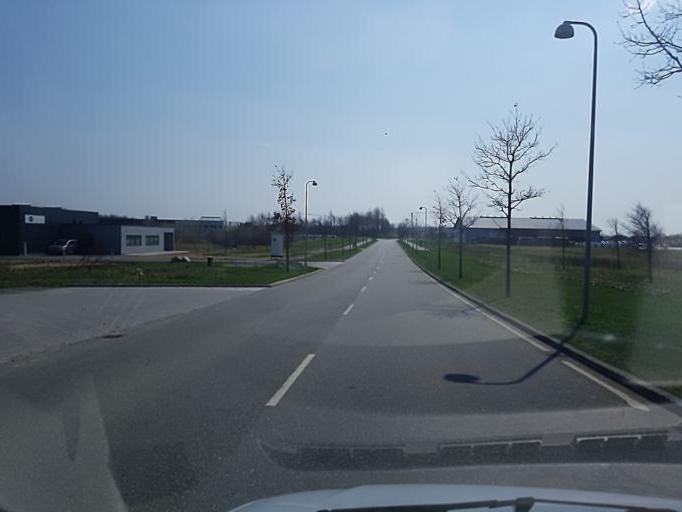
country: DK
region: South Denmark
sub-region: Odense Kommune
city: Neder Holluf
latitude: 55.3748
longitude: 10.4848
